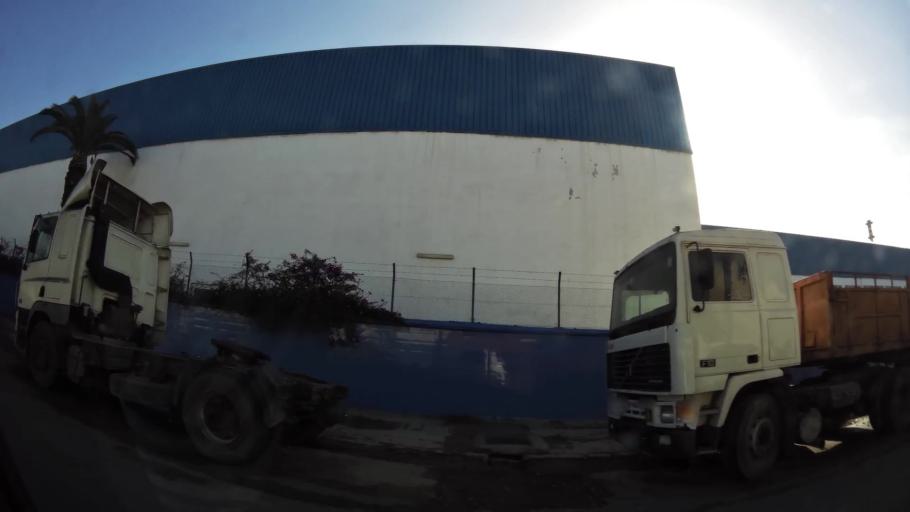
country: MA
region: Grand Casablanca
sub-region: Casablanca
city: Casablanca
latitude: 33.6037
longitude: -7.5743
